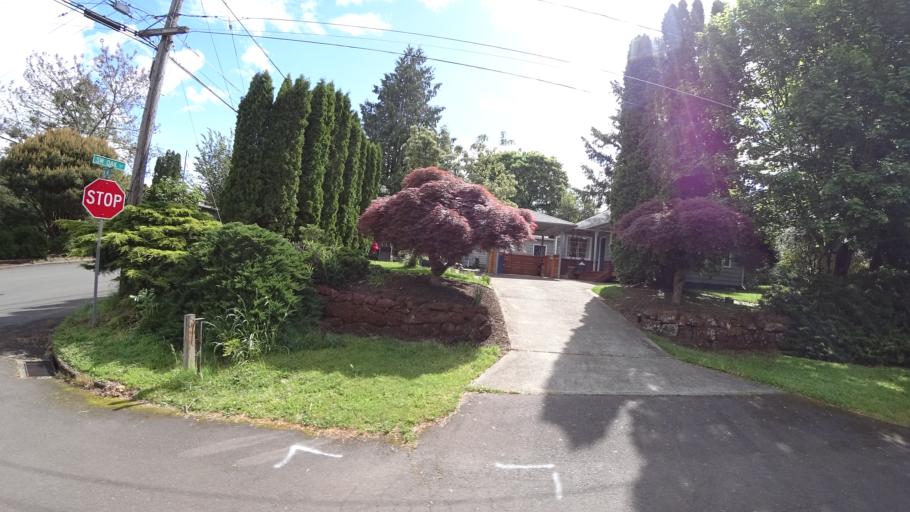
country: US
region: Oregon
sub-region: Washington County
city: Metzger
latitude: 45.4446
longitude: -122.7447
